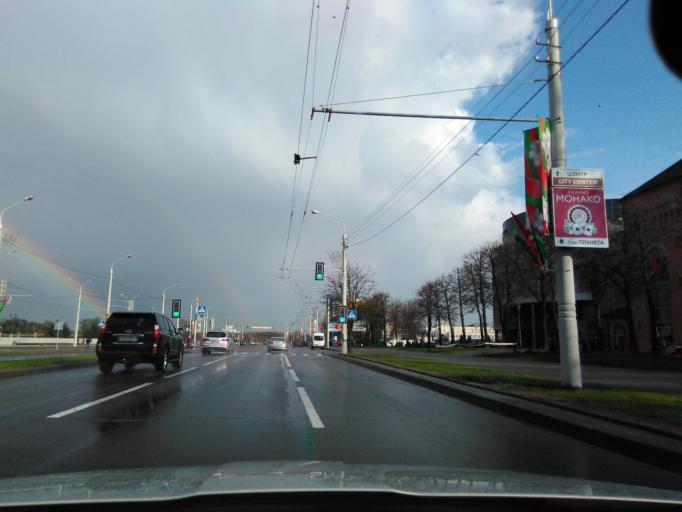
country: BY
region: Minsk
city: Minsk
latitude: 53.9273
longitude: 27.5182
